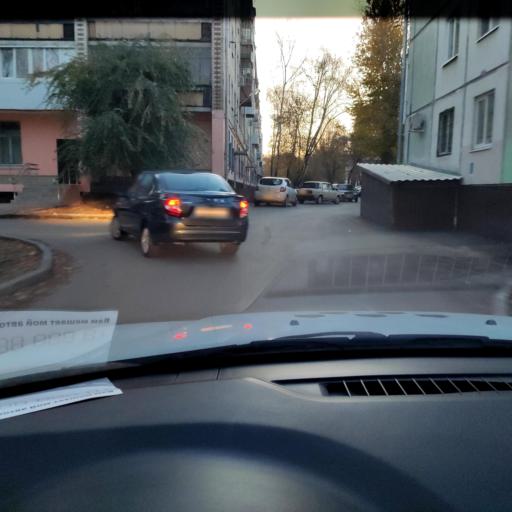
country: RU
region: Samara
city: Tol'yatti
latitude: 53.5132
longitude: 49.4292
